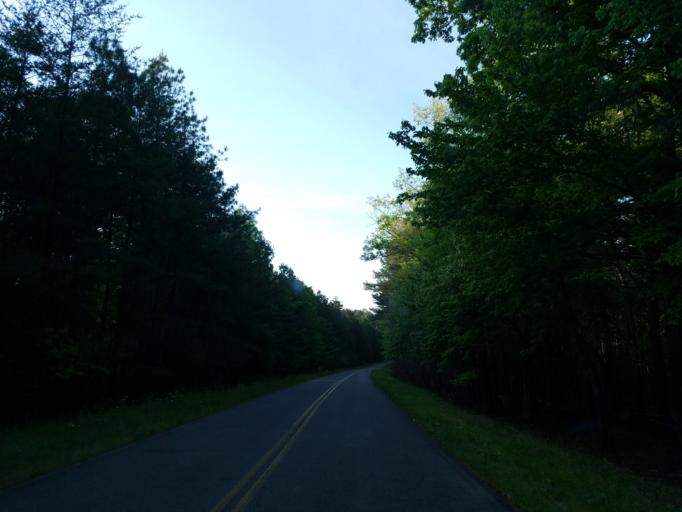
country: US
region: Georgia
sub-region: Gordon County
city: Calhoun
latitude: 34.5978
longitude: -85.0824
